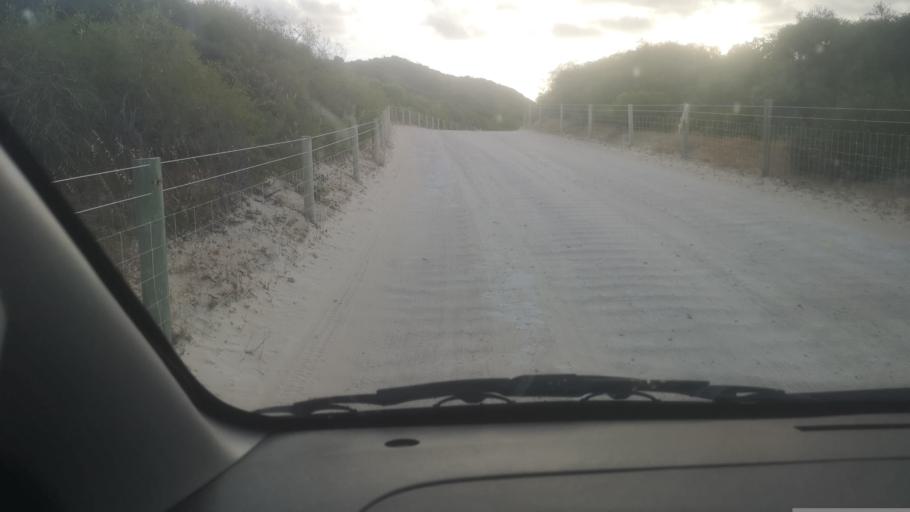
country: AU
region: Western Australia
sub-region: Wanneroo
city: Two Rocks
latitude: -31.5194
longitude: 115.6093
